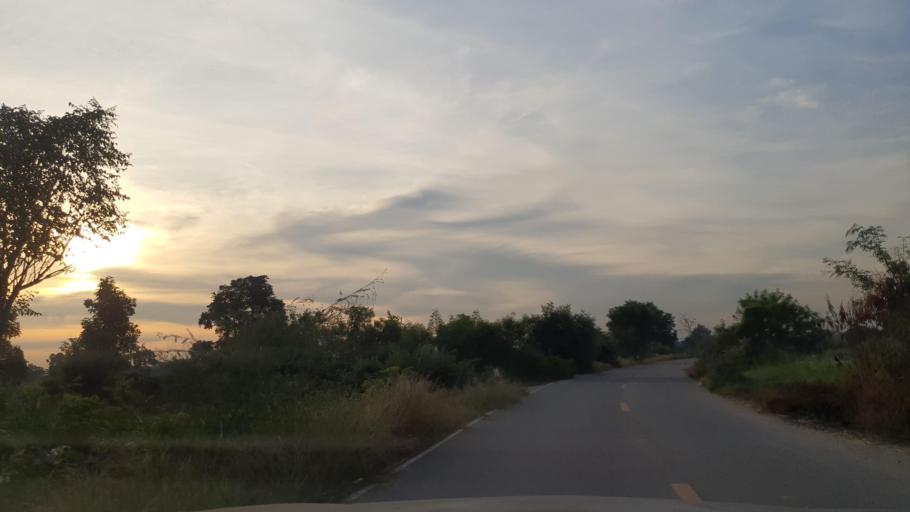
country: TH
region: Uthai Thani
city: Sawang Arom
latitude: 15.7143
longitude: 99.9564
